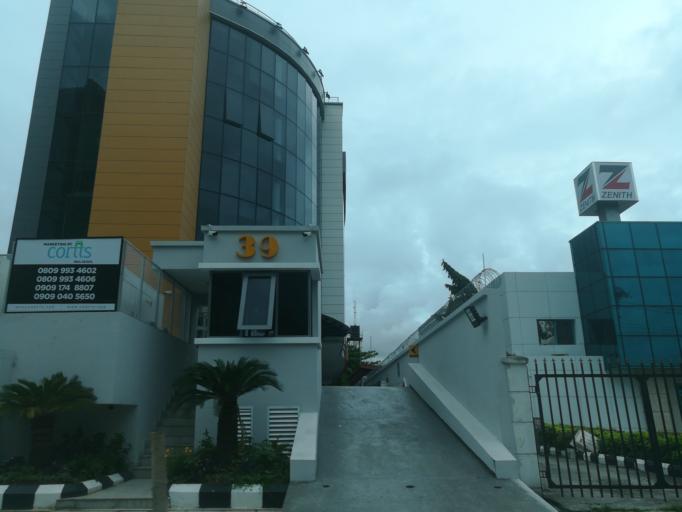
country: NG
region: Lagos
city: Ikoyi
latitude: 6.4305
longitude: 3.4177
